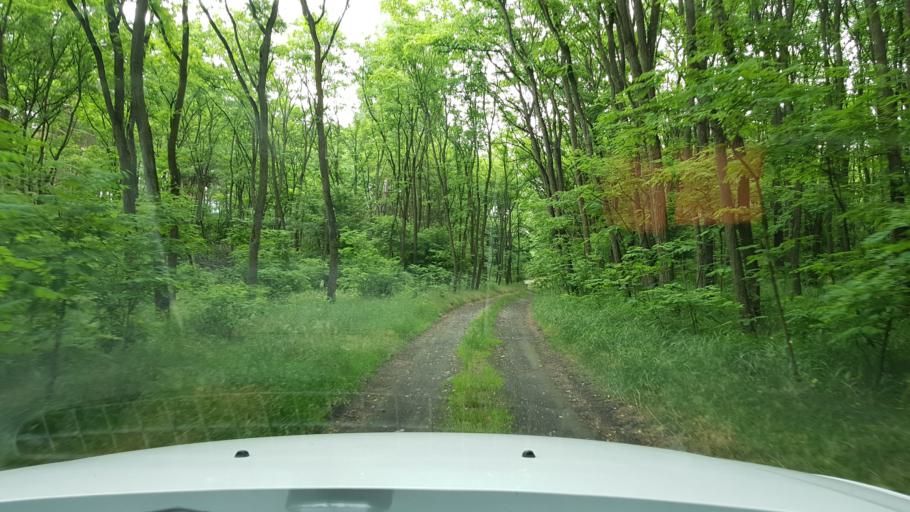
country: PL
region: West Pomeranian Voivodeship
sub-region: Powiat mysliborski
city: Boleszkowice
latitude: 52.6422
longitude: 14.5520
